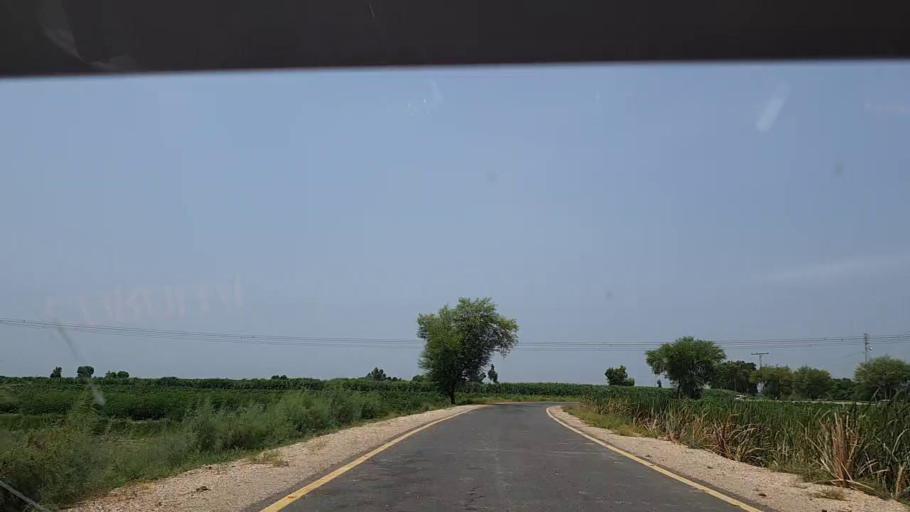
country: PK
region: Sindh
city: Adilpur
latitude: 27.8728
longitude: 69.2816
